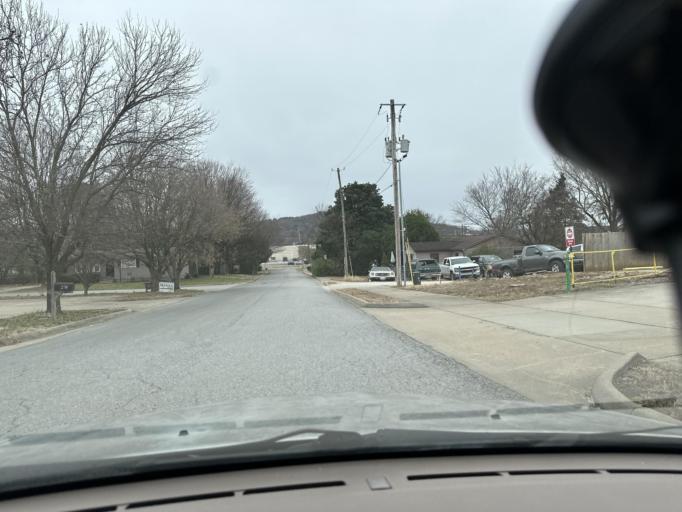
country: US
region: Arkansas
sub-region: Washington County
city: Johnson
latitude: 36.1111
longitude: -94.1434
